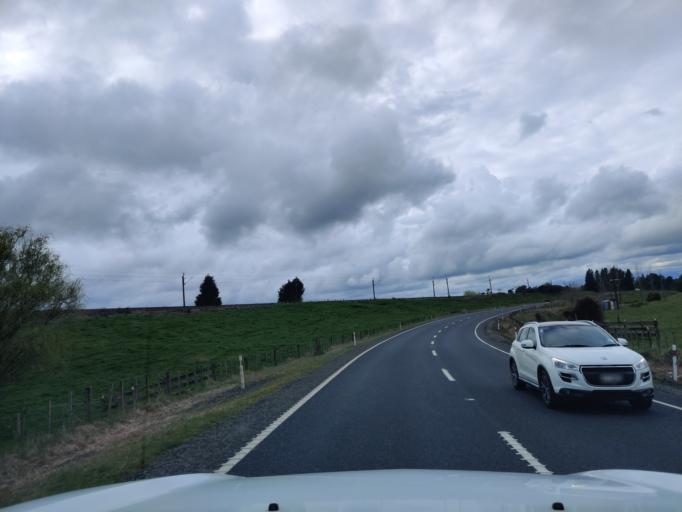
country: NZ
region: Waikato
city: Turangi
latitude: -39.0325
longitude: 175.3815
